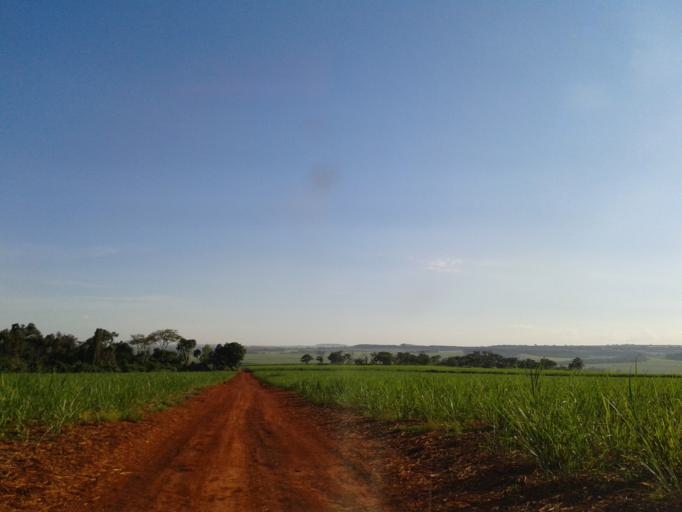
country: BR
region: Minas Gerais
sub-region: Centralina
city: Centralina
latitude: -18.6644
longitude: -49.2579
